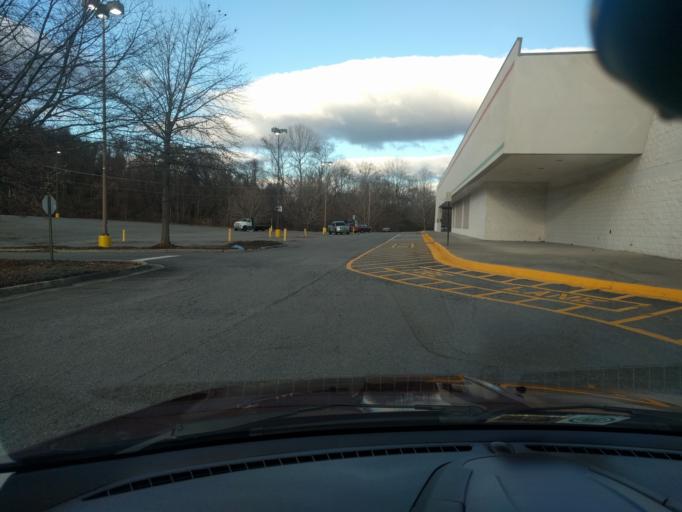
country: US
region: Virginia
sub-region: City of Bedford
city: Bedford
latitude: 37.3374
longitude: -79.5332
